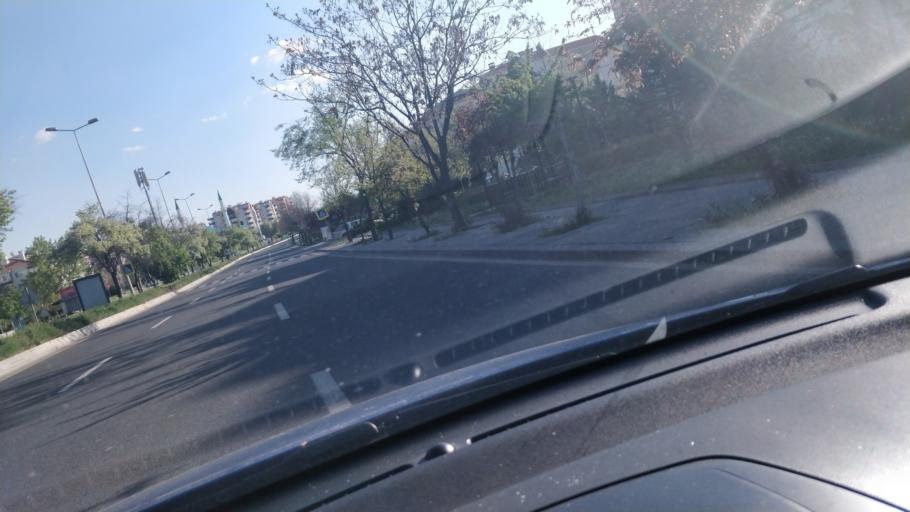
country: TR
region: Ankara
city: Batikent
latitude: 39.9572
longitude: 32.7200
